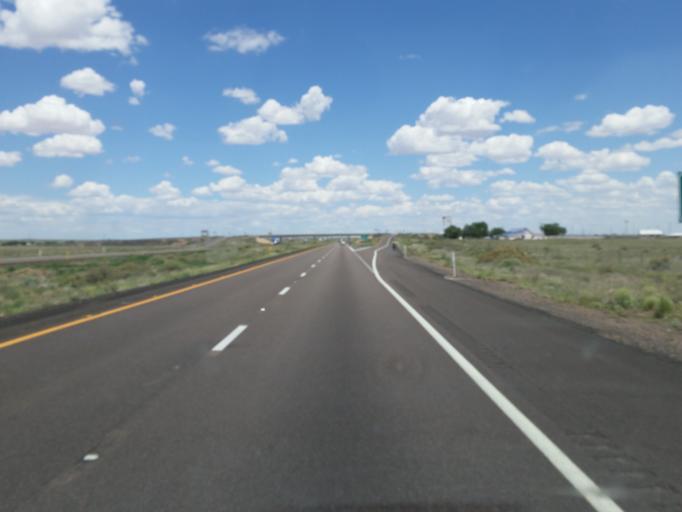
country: US
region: Arizona
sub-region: Navajo County
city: Holbrook
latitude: 34.9789
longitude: -110.0636
